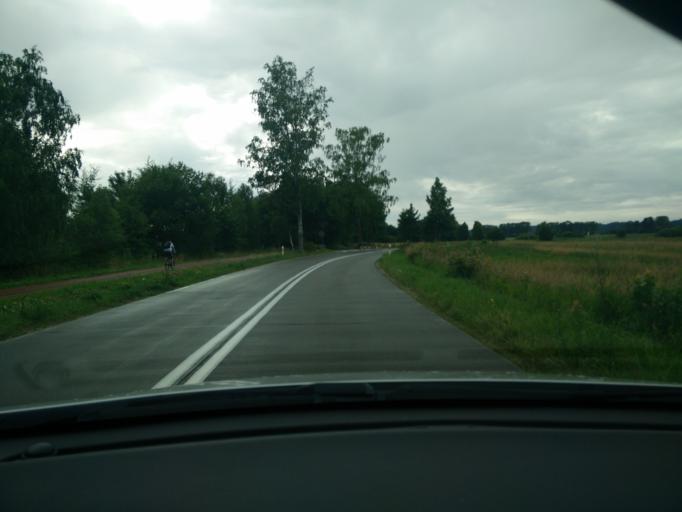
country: PL
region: Pomeranian Voivodeship
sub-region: Powiat pucki
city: Mrzezino
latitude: 54.6222
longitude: 18.4416
